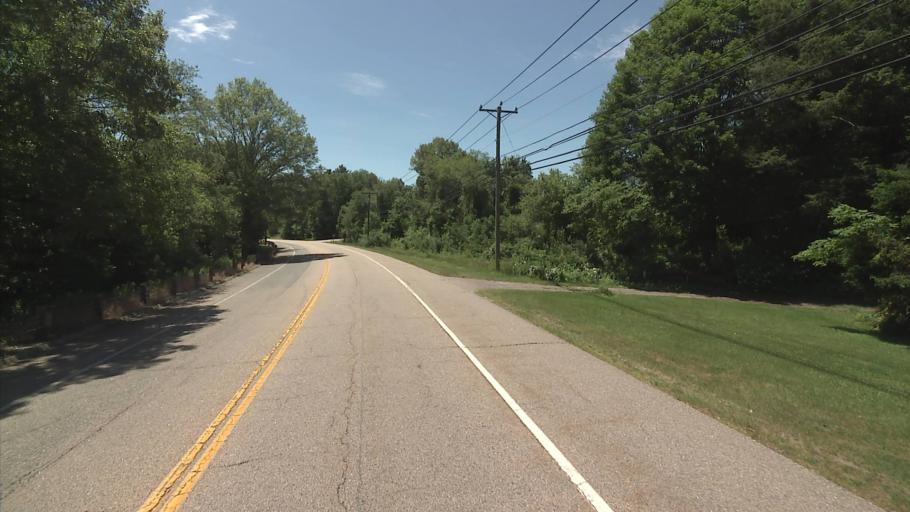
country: US
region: Connecticut
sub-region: New London County
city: Pawcatuck
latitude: 41.4144
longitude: -71.8454
